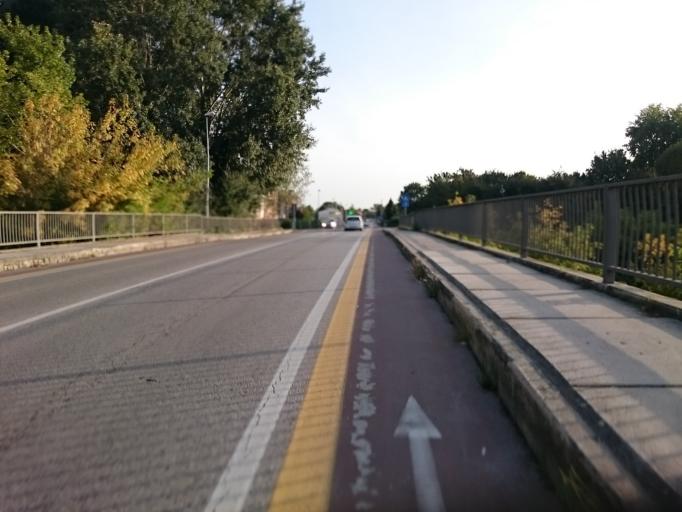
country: IT
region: Veneto
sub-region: Provincia di Padova
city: Padova
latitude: 45.4049
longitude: 11.9119
